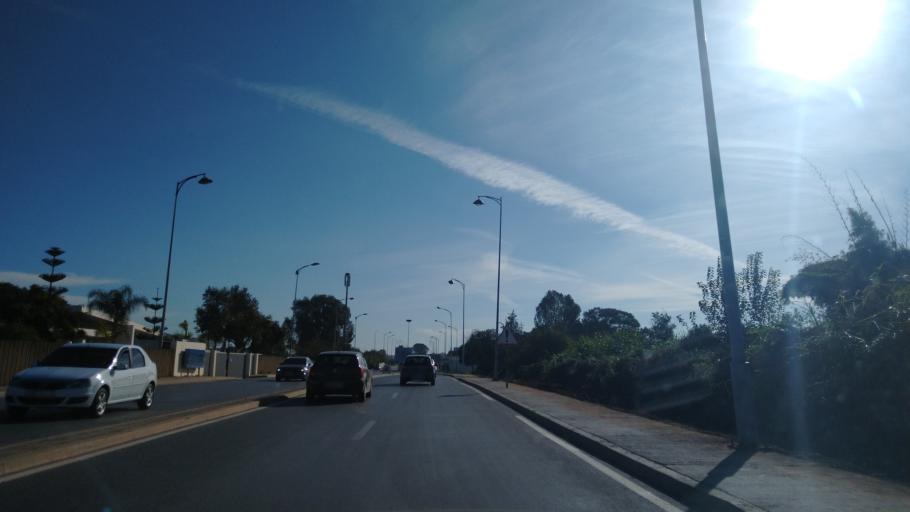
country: MA
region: Rabat-Sale-Zemmour-Zaer
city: Sale
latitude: 34.0223
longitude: -6.7348
